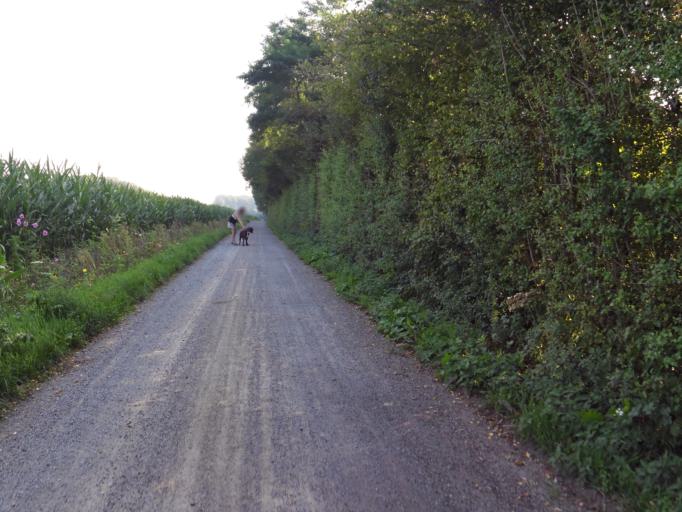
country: DE
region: North Rhine-Westphalia
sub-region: Regierungsbezirk Munster
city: Billerbeck
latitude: 51.9755
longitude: 7.3261
